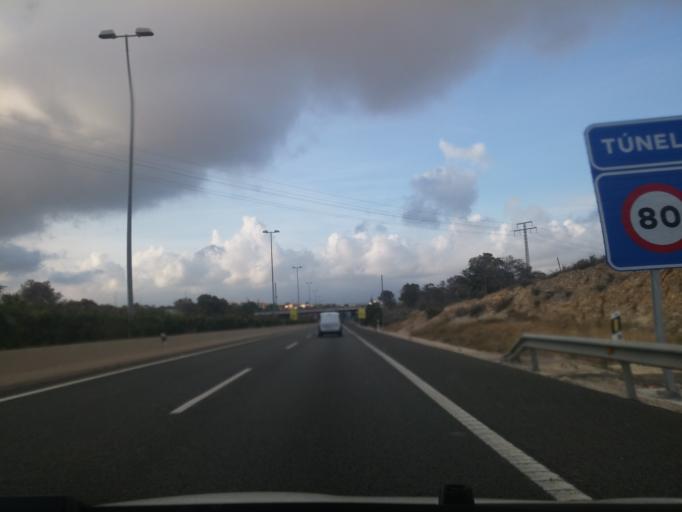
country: ES
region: Valencia
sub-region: Provincia de Alicante
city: San Juan de Alicante
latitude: 38.3981
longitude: -0.4499
